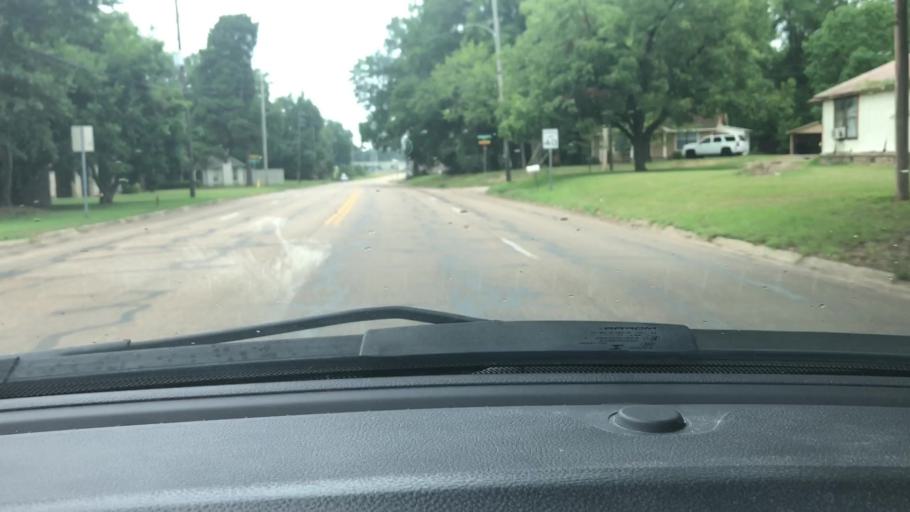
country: US
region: Texas
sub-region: Bowie County
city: Wake Village
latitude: 33.4347
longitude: -94.0905
